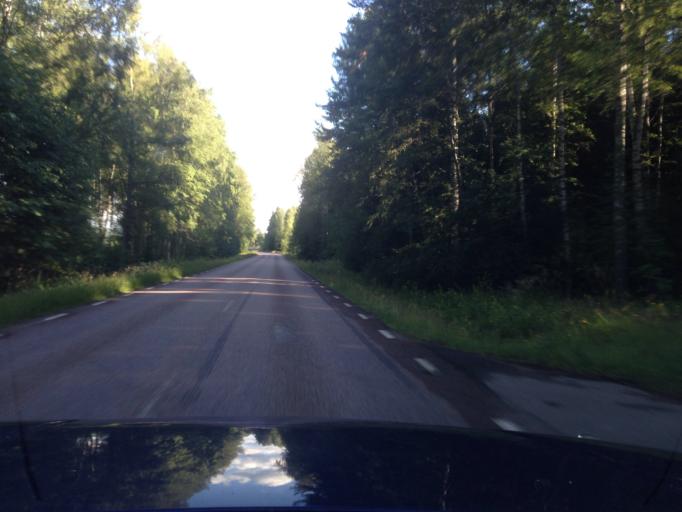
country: SE
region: Dalarna
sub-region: Ludvika Kommun
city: Grangesberg
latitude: 60.1926
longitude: 14.9682
